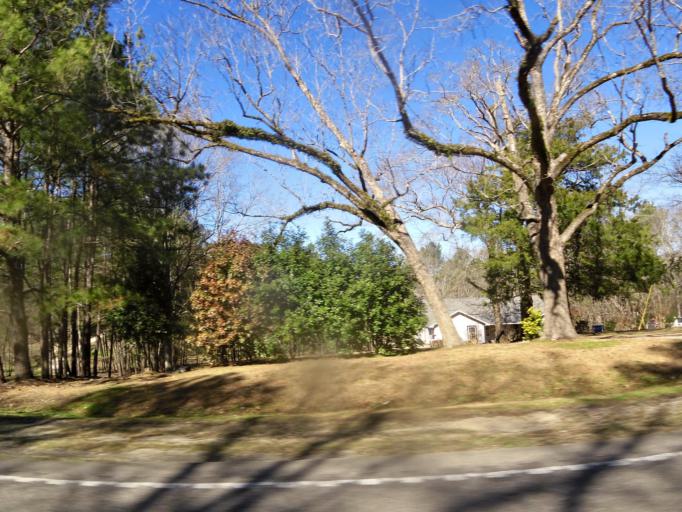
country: US
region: Alabama
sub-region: Bullock County
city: Union Springs
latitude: 32.1370
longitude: -85.7356
